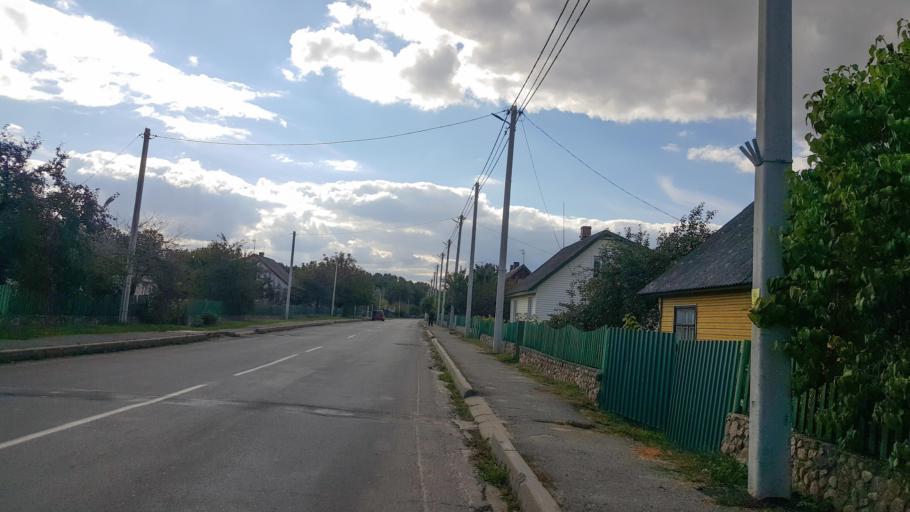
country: BY
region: Brest
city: Kamyanyets
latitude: 52.4034
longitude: 23.8111
